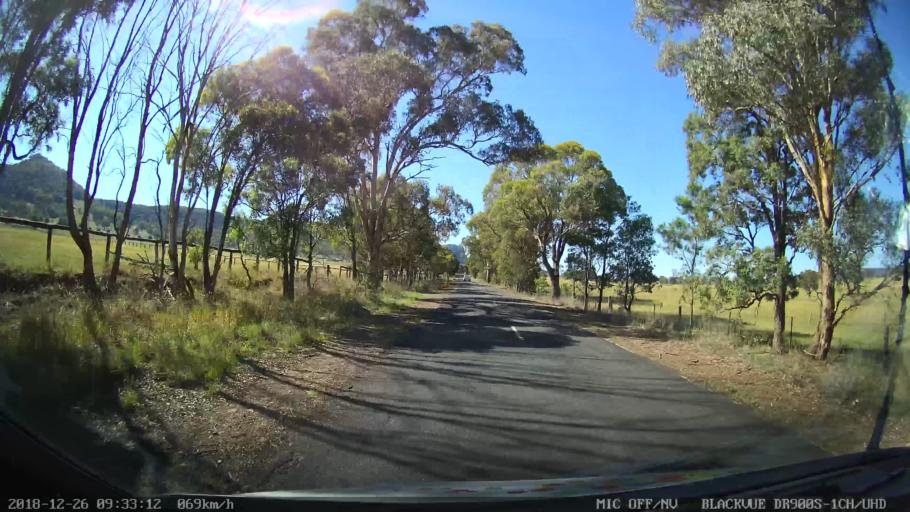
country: AU
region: New South Wales
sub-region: Mid-Western Regional
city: Kandos
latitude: -32.8923
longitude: 150.0341
